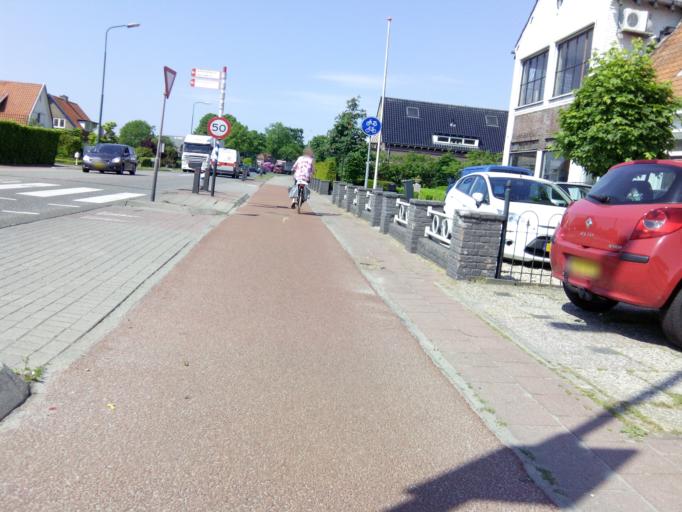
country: NL
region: Utrecht
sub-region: Gemeente Woudenberg
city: Woudenberg
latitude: 52.0794
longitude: 5.4450
